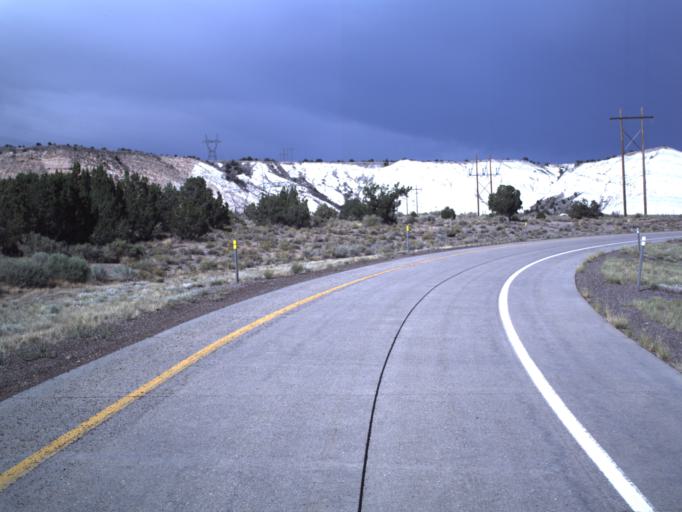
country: US
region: Utah
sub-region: Sevier County
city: Monroe
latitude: 38.6021
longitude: -112.2542
